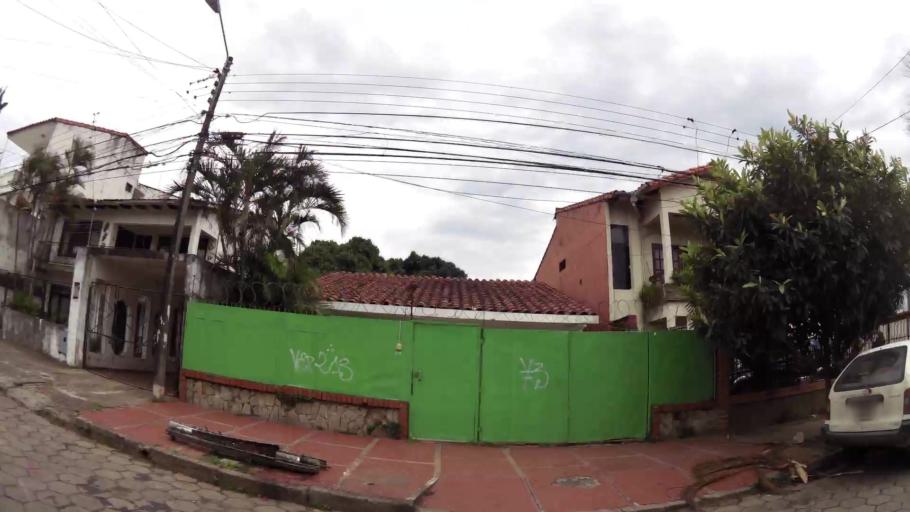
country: BO
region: Santa Cruz
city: Santa Cruz de la Sierra
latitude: -17.7721
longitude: -63.1702
